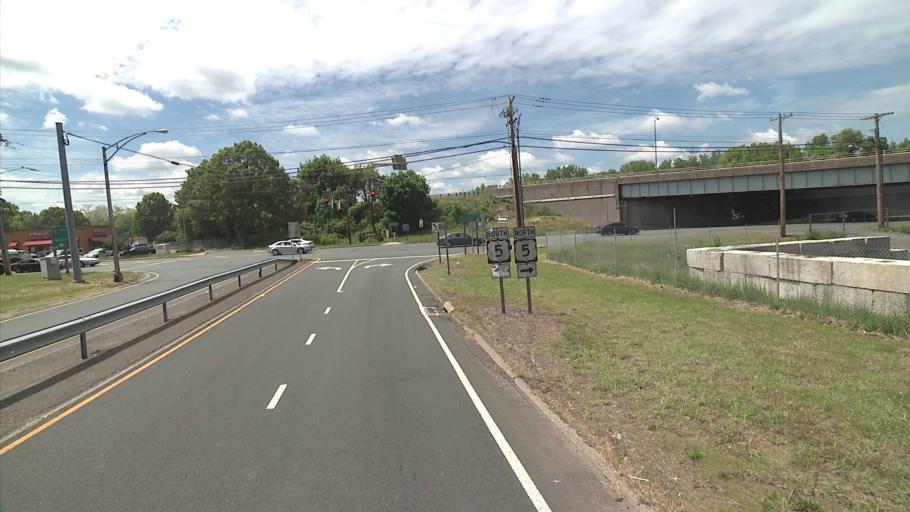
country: US
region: Connecticut
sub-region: New Haven County
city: North Haven
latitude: 41.3987
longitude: -72.8518
